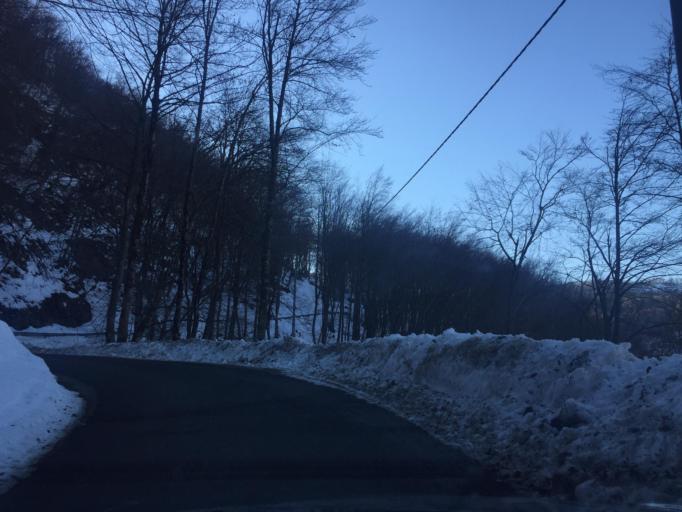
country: IT
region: Friuli Venezia Giulia
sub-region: Provincia di Udine
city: Lauco
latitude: 46.4358
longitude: 12.9714
